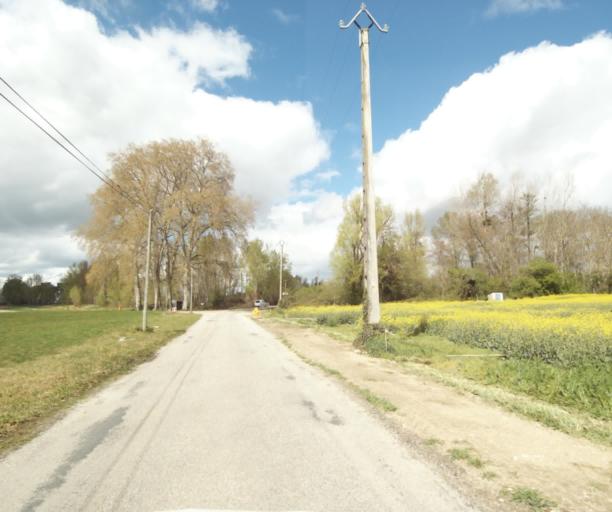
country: FR
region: Midi-Pyrenees
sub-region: Departement de l'Ariege
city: Saverdun
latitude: 43.2494
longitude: 1.5823
